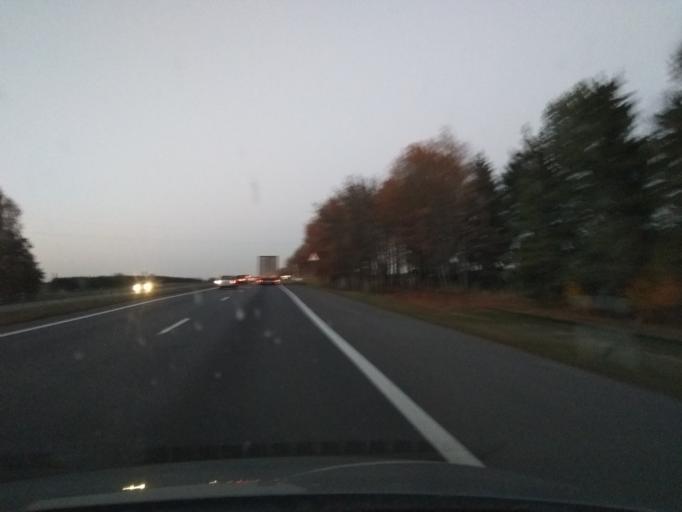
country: BY
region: Minsk
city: Enyerhyetykaw
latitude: 53.6391
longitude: 27.0658
